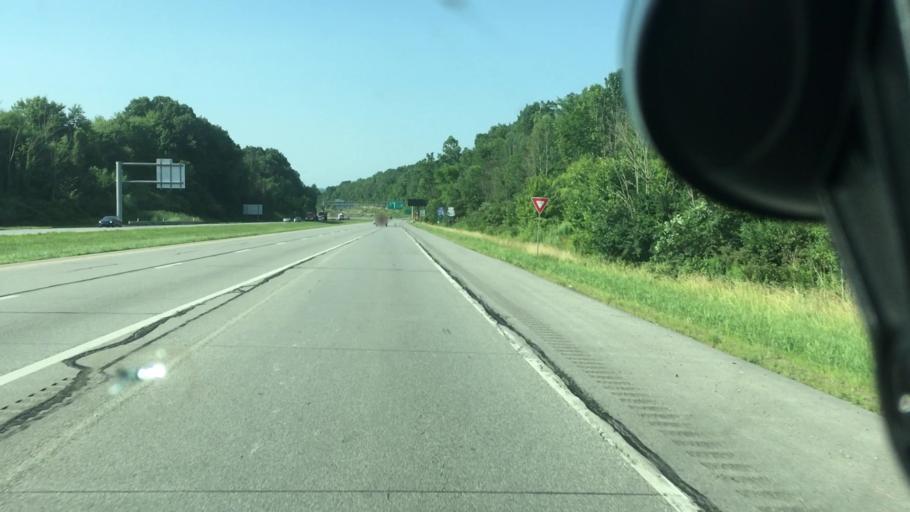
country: US
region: Pennsylvania
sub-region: Lawrence County
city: Oakwood
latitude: 41.0074
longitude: -80.3921
